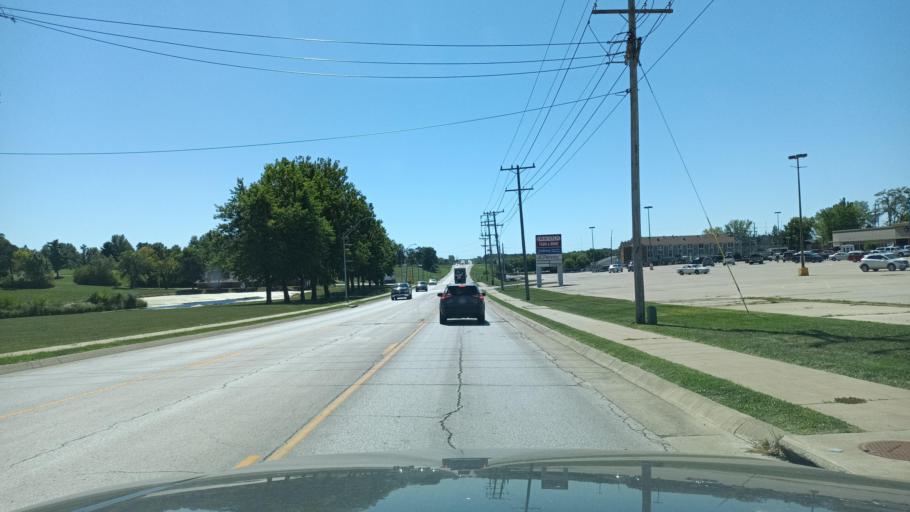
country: US
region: Missouri
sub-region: Adair County
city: Kirksville
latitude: 40.1774
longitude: -92.5720
